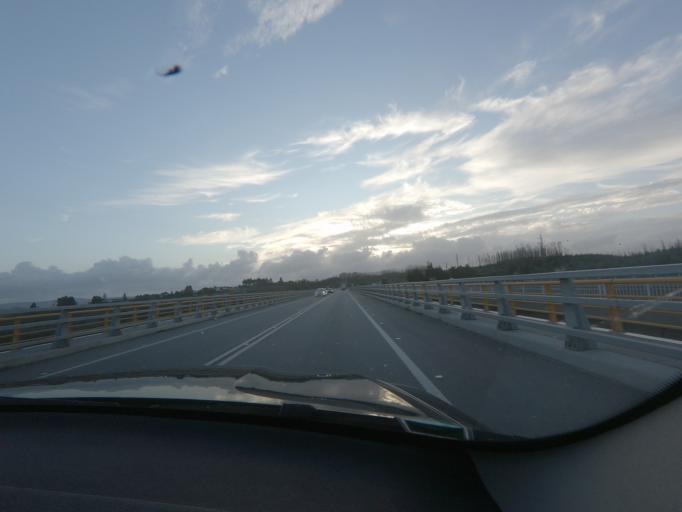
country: PT
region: Viseu
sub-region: Mortagua
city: Mortagua
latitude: 40.3479
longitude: -8.1818
